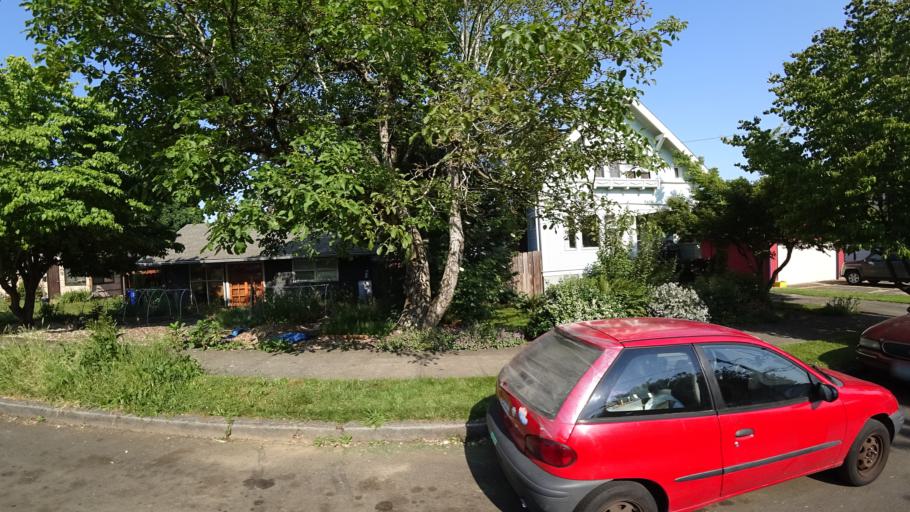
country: US
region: Oregon
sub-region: Washington County
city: West Haven
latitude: 45.5952
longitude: -122.7390
